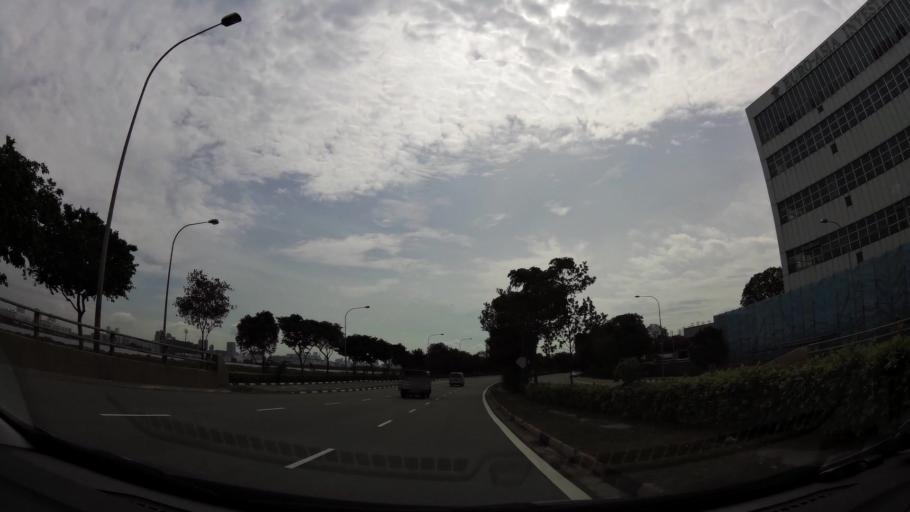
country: SG
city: Singapore
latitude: 1.3108
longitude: 103.7367
